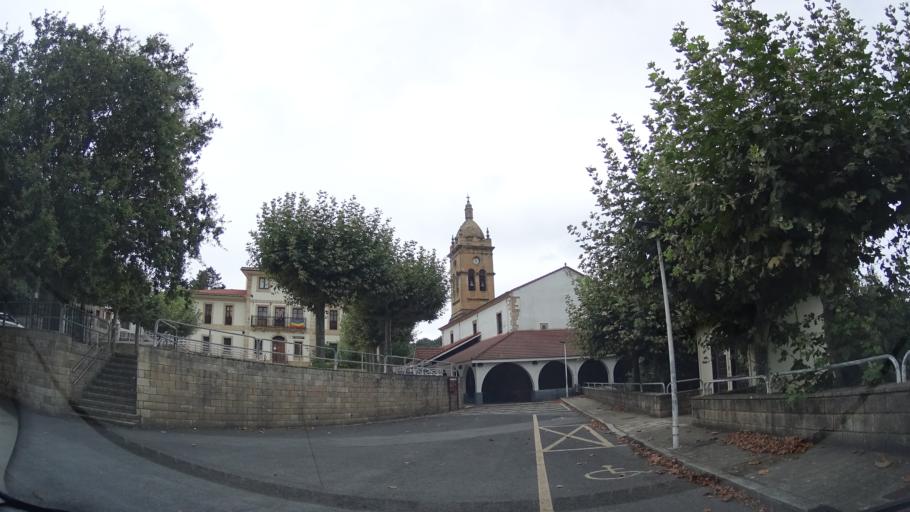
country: ES
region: Basque Country
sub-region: Bizkaia
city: Plentzia
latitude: 43.4076
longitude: -2.9648
